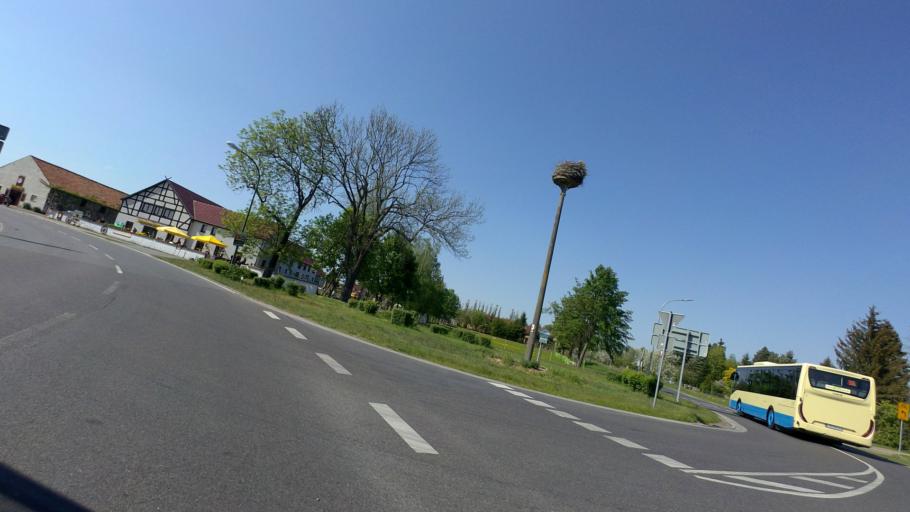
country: DE
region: Brandenburg
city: Schlepzig
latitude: 52.0796
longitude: 13.8942
